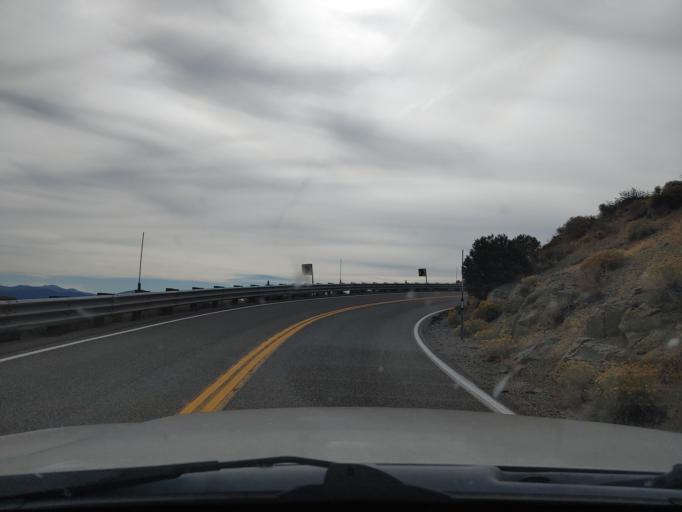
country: US
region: Nevada
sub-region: Storey County
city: Virginia City
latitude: 39.2861
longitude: -119.6357
